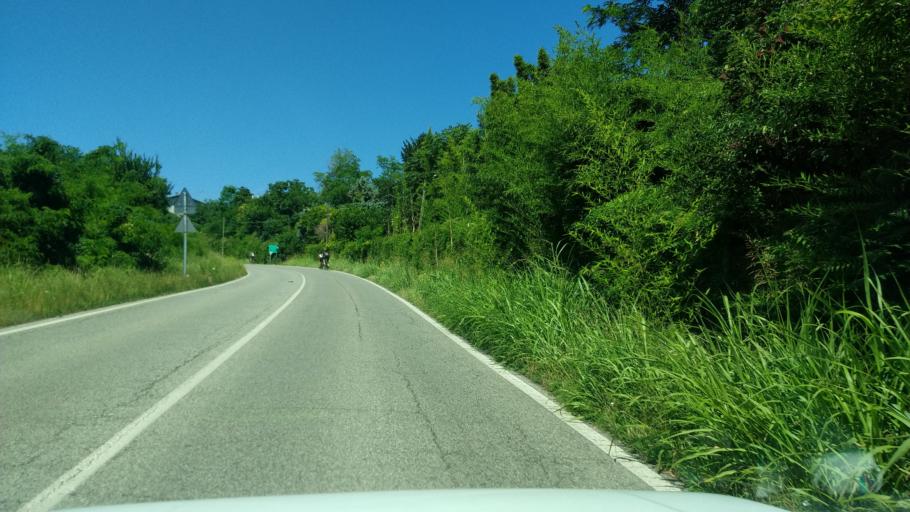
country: IT
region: Veneto
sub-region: Provincia di Vicenza
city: Breganze
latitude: 45.7108
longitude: 11.5786
